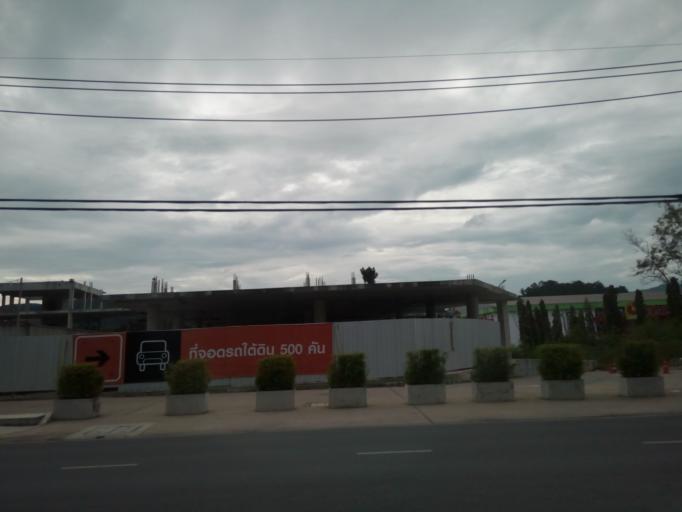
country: TH
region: Phuket
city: Wichit
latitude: 7.8937
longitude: 98.3692
